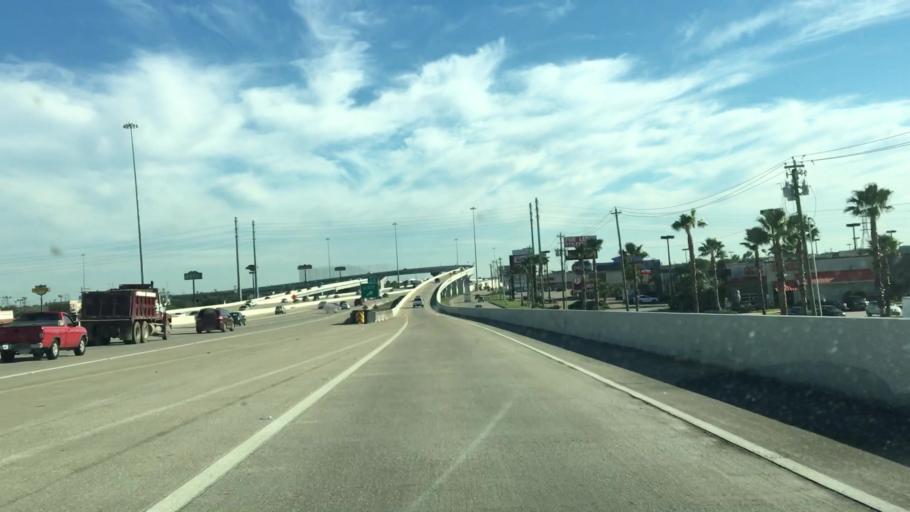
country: US
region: Texas
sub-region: Harris County
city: Webster
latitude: 29.5272
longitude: -95.1273
